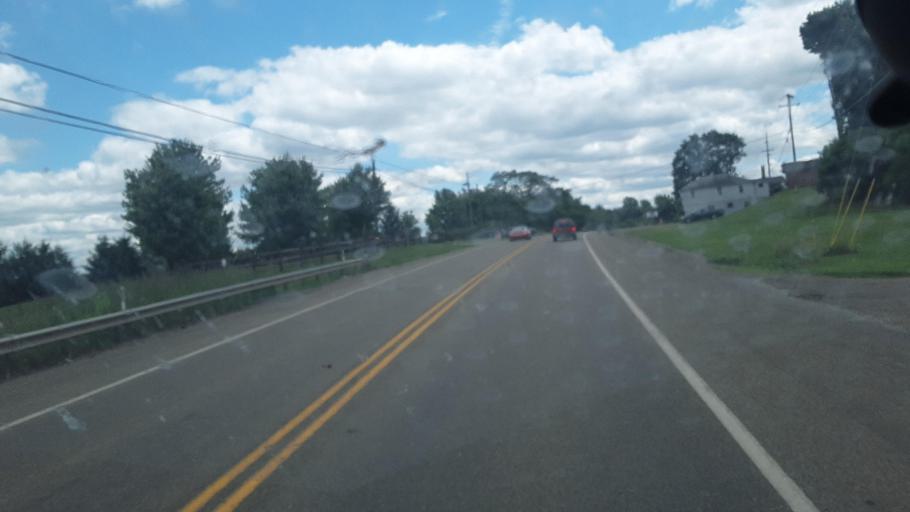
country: US
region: Pennsylvania
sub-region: Butler County
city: Prospect
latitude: 40.9580
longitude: -80.1555
